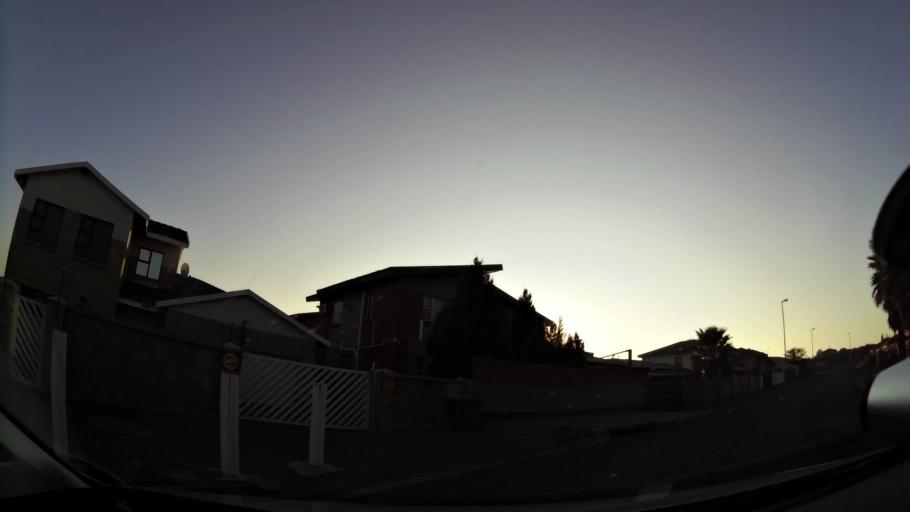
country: ZA
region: Orange Free State
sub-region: Mangaung Metropolitan Municipality
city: Bloemfontein
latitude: -29.0955
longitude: 26.1643
